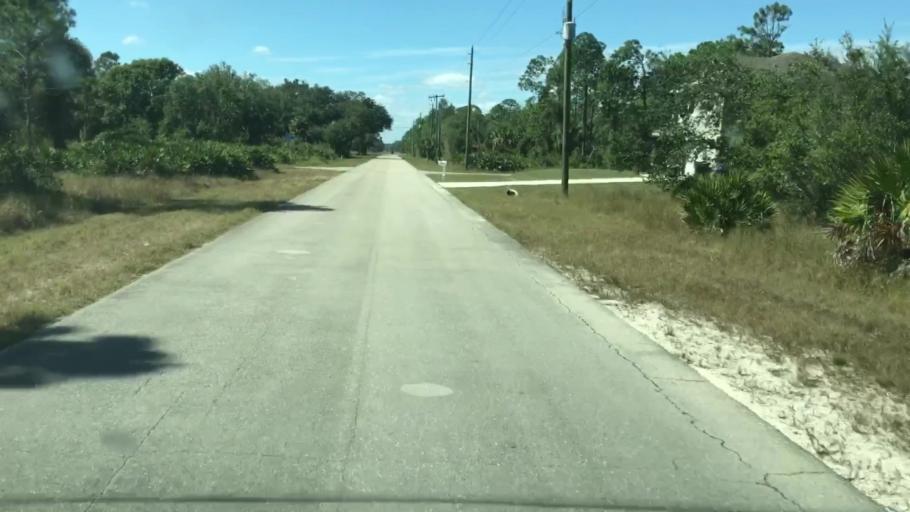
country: US
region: Florida
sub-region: Lee County
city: Lehigh Acres
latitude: 26.6619
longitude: -81.6221
